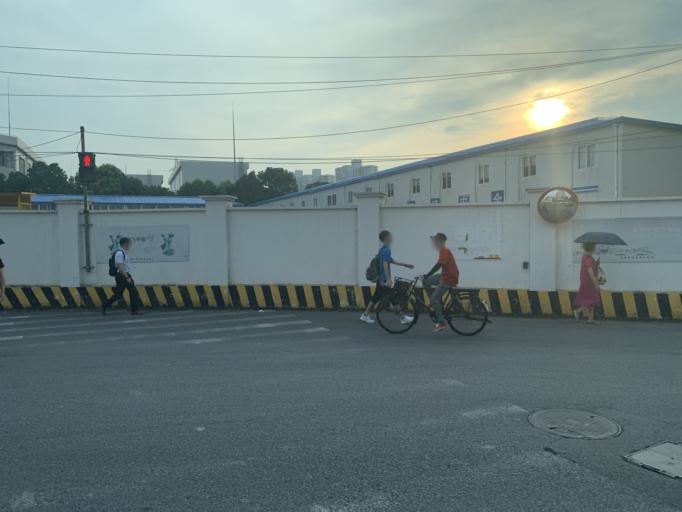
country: CN
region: Shanghai Shi
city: Huamu
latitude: 31.2437
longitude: 121.5731
